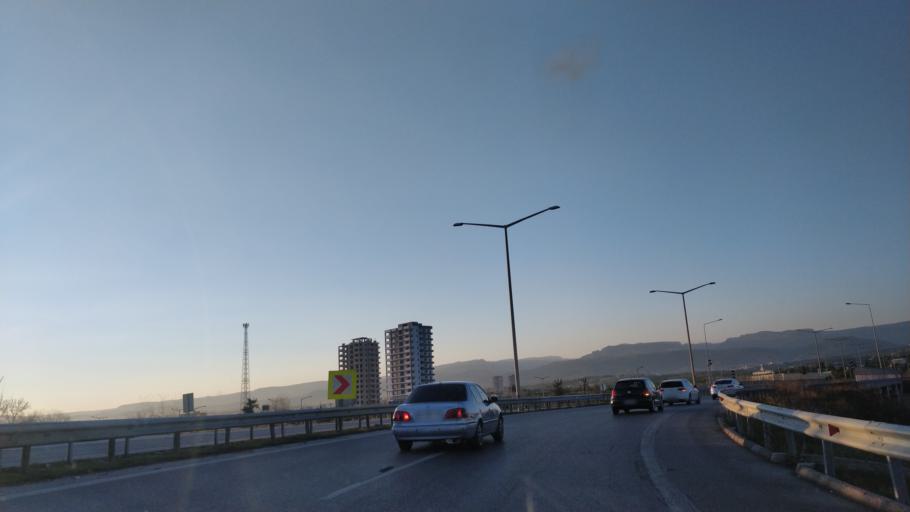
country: TR
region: Mersin
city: Tomuk
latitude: 36.6906
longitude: 34.4356
